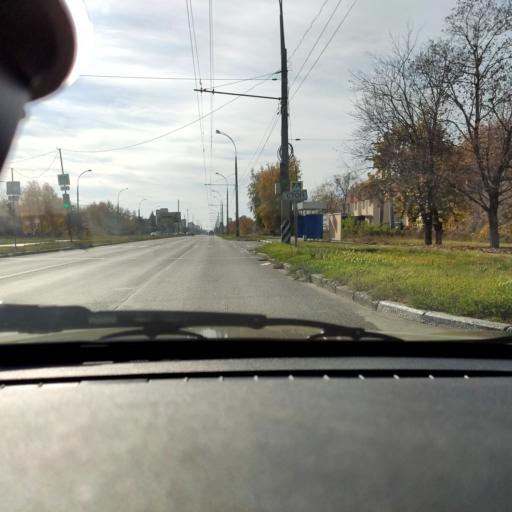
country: RU
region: Samara
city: Tol'yatti
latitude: 53.5436
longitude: 49.3008
